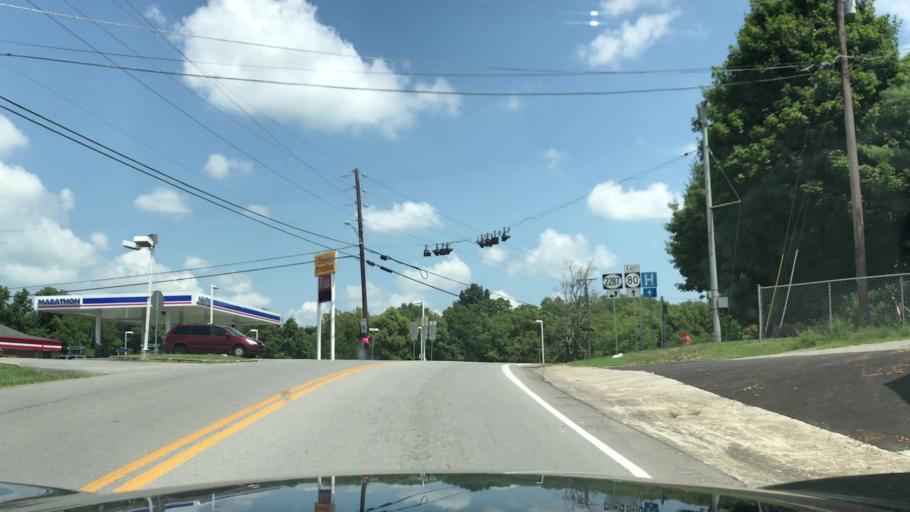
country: US
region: Kentucky
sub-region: Adair County
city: Columbia
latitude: 37.0983
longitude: -85.3140
